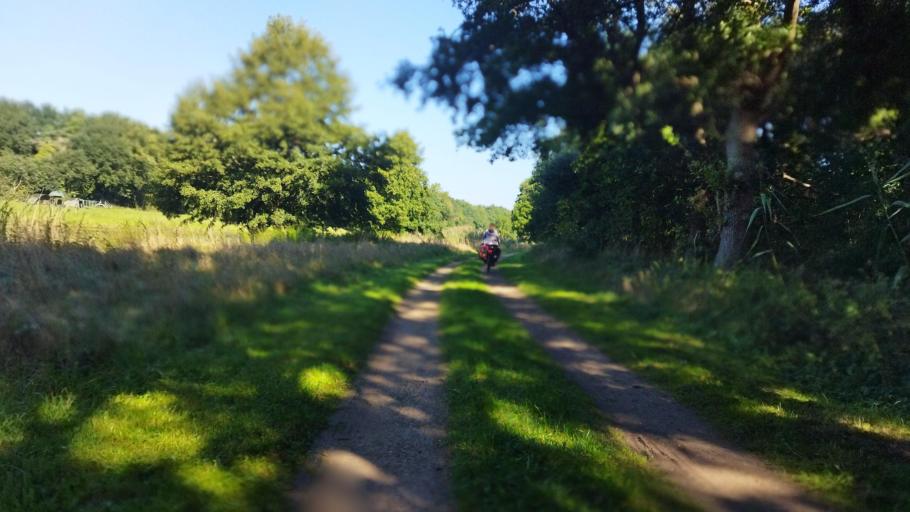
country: DE
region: Lower Saxony
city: Haren
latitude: 52.7671
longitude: 7.2545
